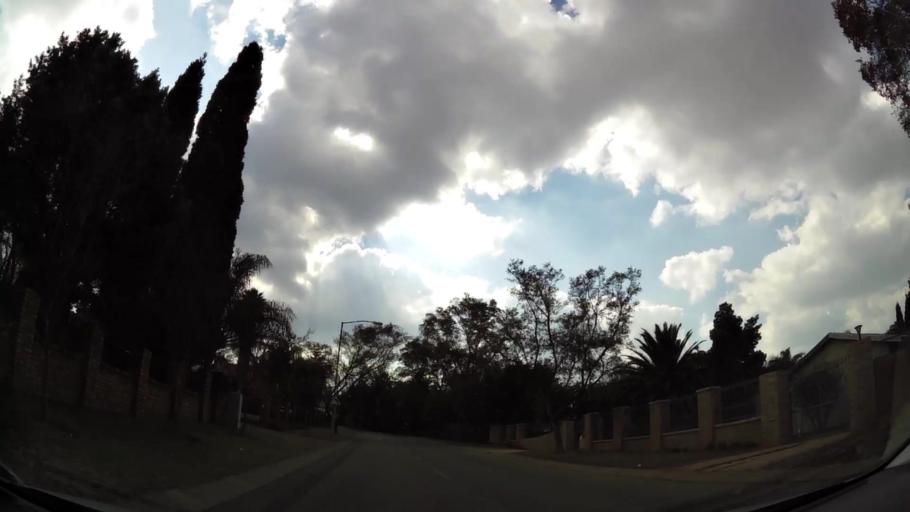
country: ZA
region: Gauteng
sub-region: City of Tshwane Metropolitan Municipality
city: Centurion
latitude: -25.8432
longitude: 28.2712
